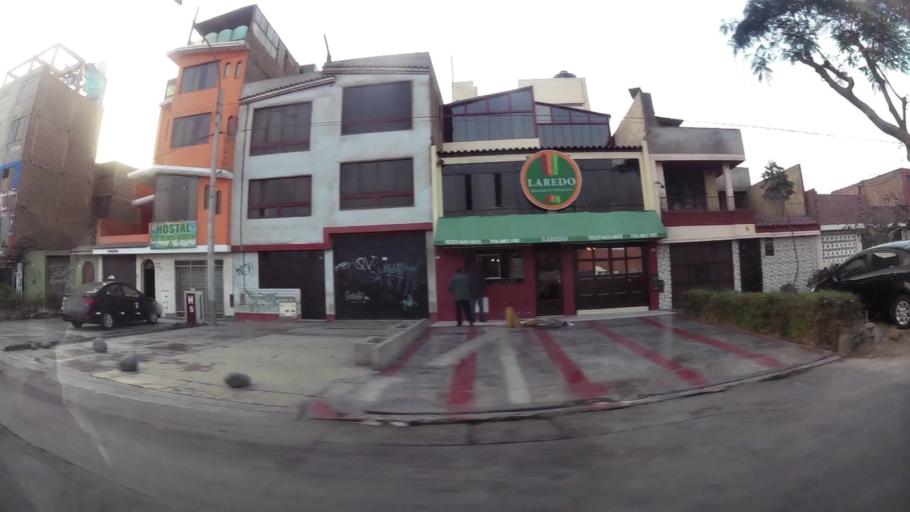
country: PE
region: Lima
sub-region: Lima
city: Independencia
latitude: -12.0086
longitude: -77.0648
